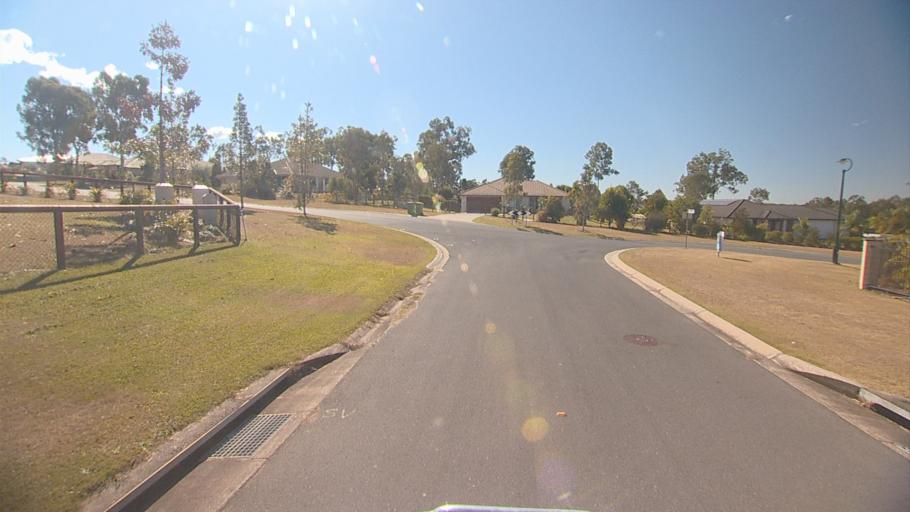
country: AU
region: Queensland
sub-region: Logan
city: North Maclean
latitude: -27.7580
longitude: 152.9456
